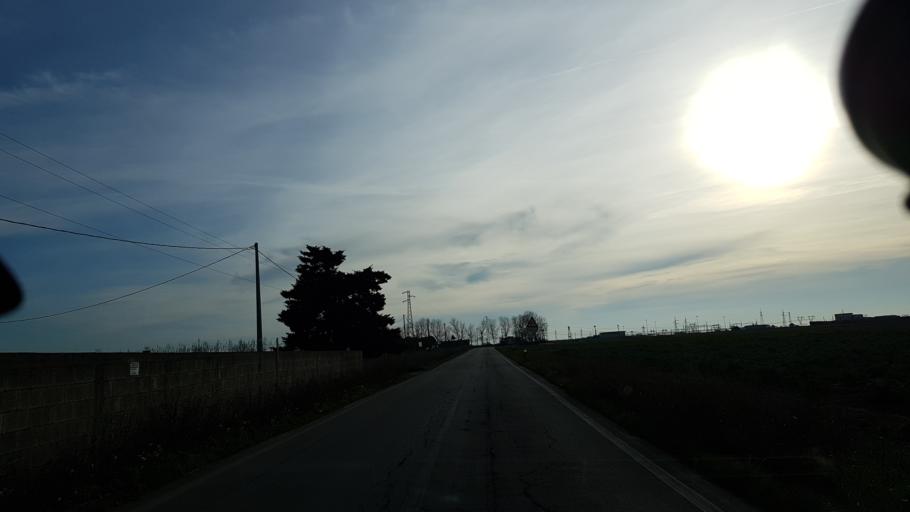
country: IT
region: Apulia
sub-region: Provincia di Brindisi
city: Brindisi
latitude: 40.6107
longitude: 17.9138
